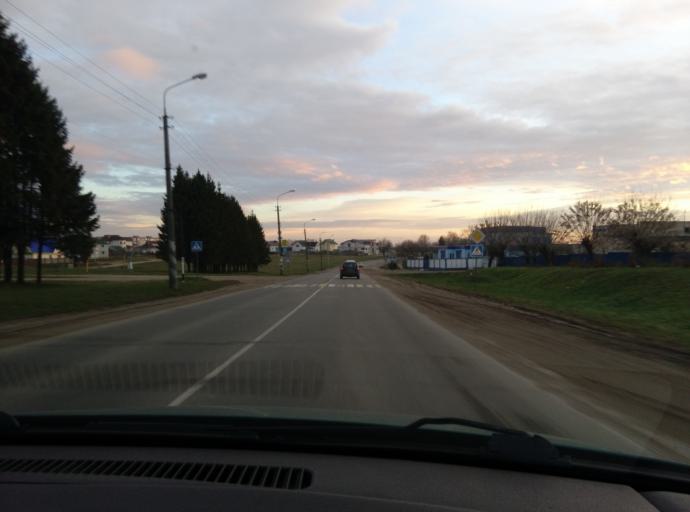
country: BY
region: Minsk
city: Horad Barysaw
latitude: 54.2659
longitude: 28.5001
